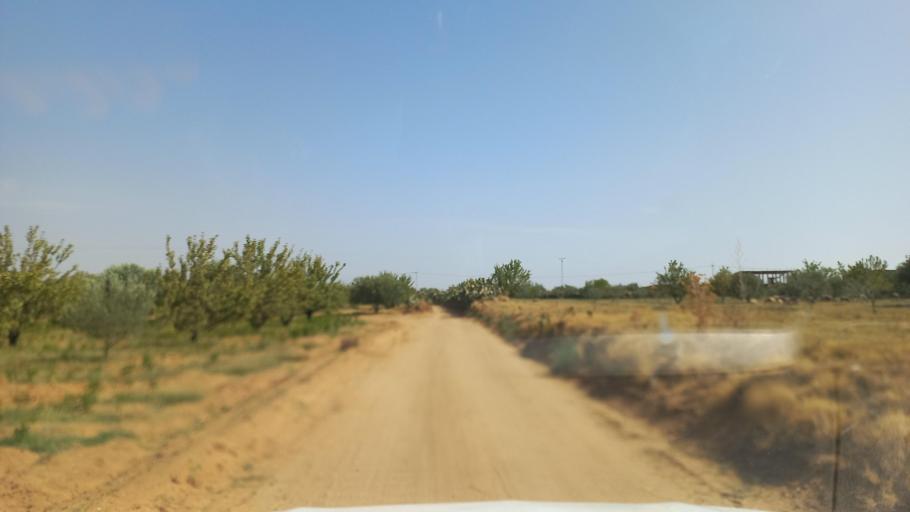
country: TN
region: Al Qasrayn
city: Kasserine
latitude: 35.2350
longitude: 9.0440
